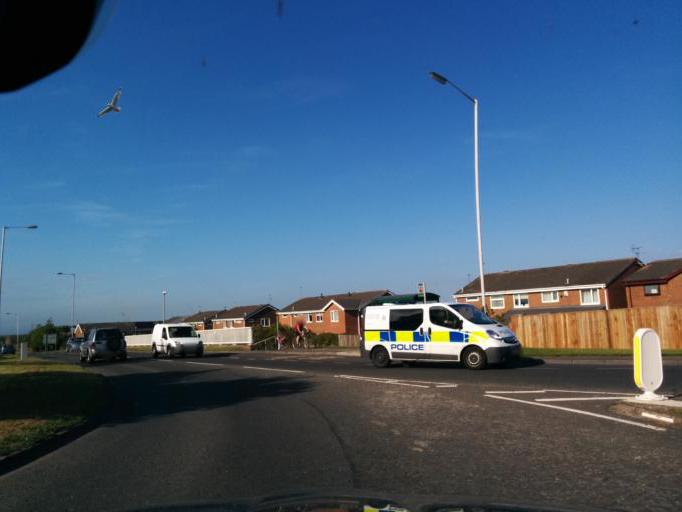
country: GB
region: England
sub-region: Northumberland
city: Cramlington
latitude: 55.0883
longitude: -1.5779
